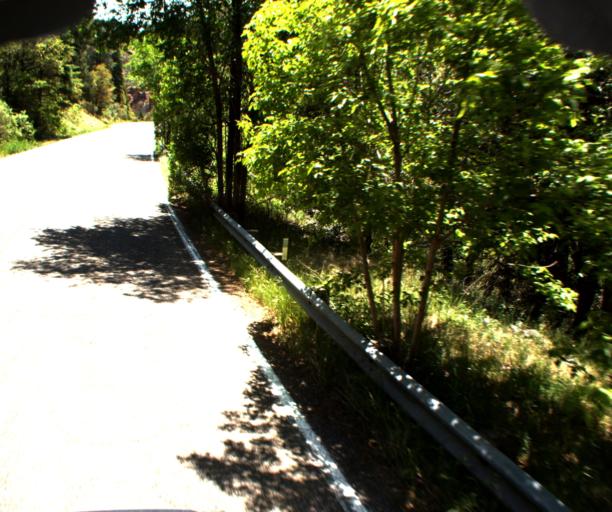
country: US
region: Arizona
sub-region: Coconino County
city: Sedona
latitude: 34.9588
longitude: -111.7536
